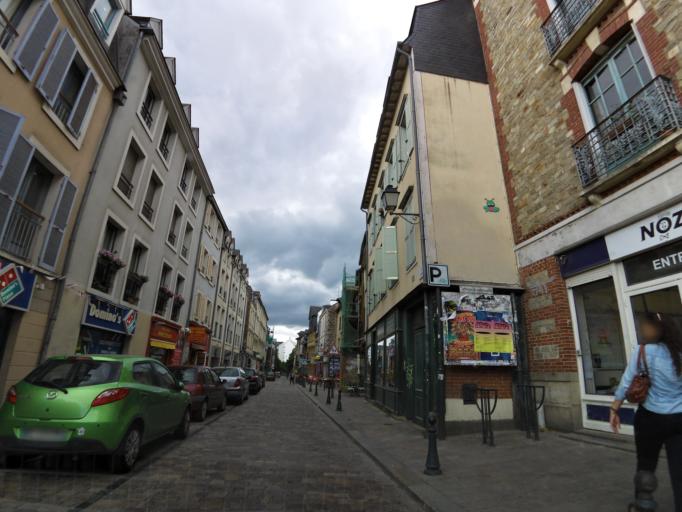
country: FR
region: Brittany
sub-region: Departement d'Ille-et-Vilaine
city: Rennes
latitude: 48.1157
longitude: -1.6809
